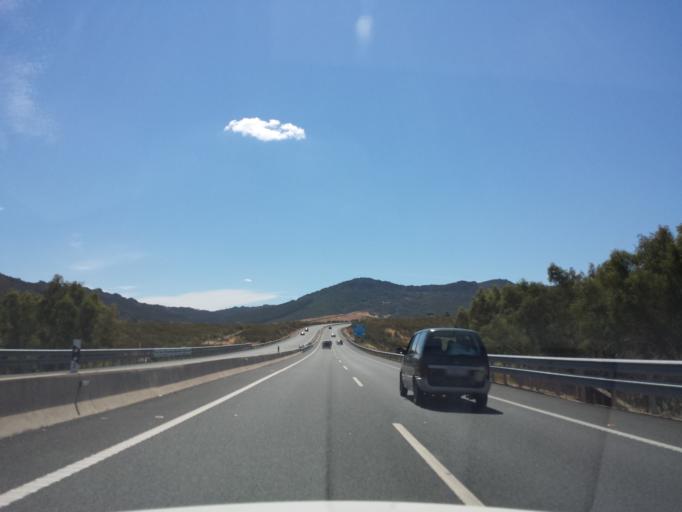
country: ES
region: Extremadura
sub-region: Provincia de Caceres
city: Romangordo
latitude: 39.7119
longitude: -5.6961
